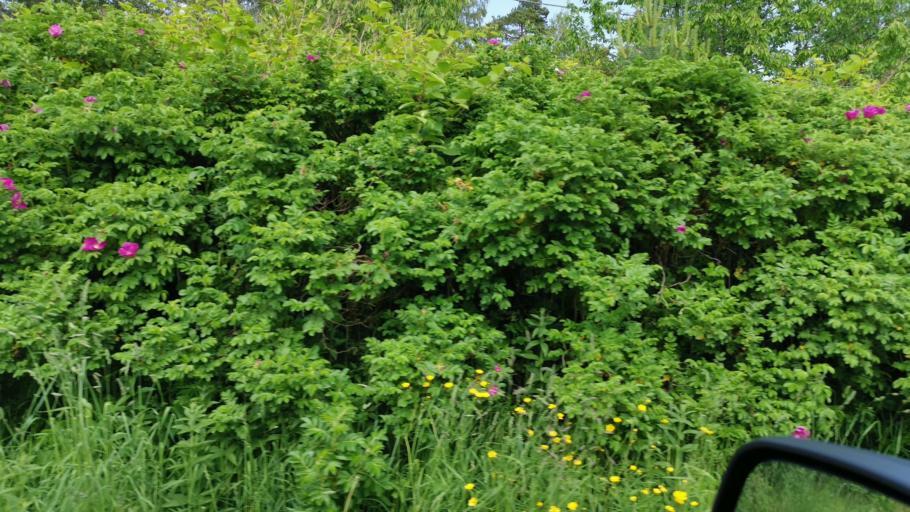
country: SE
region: Vaestra Goetaland
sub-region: Orust
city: Henan
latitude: 58.3108
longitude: 11.7017
